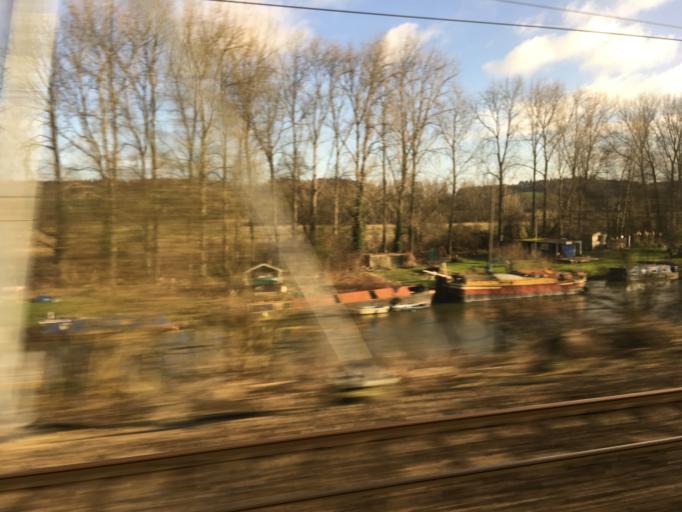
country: GB
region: England
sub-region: West Berkshire
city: Tilehurst
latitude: 51.4757
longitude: -1.0379
